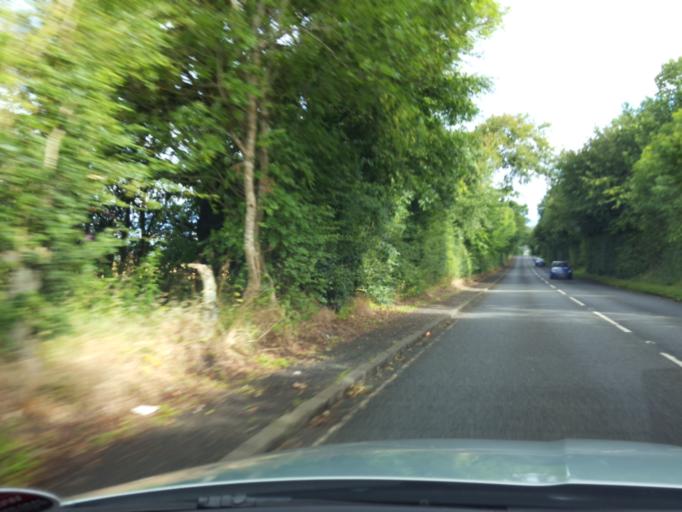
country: GB
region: Scotland
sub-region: Falkirk
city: Bo'ness
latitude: 55.9982
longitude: -3.6083
